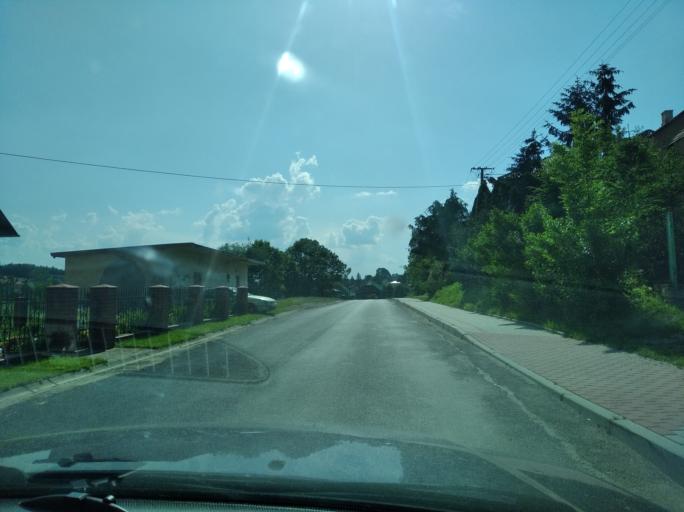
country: PL
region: Subcarpathian Voivodeship
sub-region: Powiat jaroslawski
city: Rokietnica
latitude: 49.9257
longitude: 22.6976
